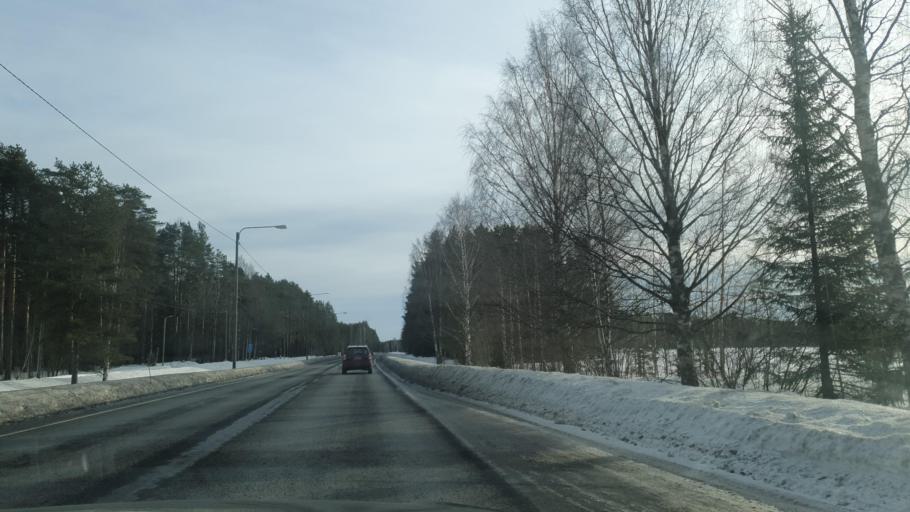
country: FI
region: Northern Ostrobothnia
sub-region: Oulu
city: Muhos
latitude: 64.8801
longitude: 25.8501
